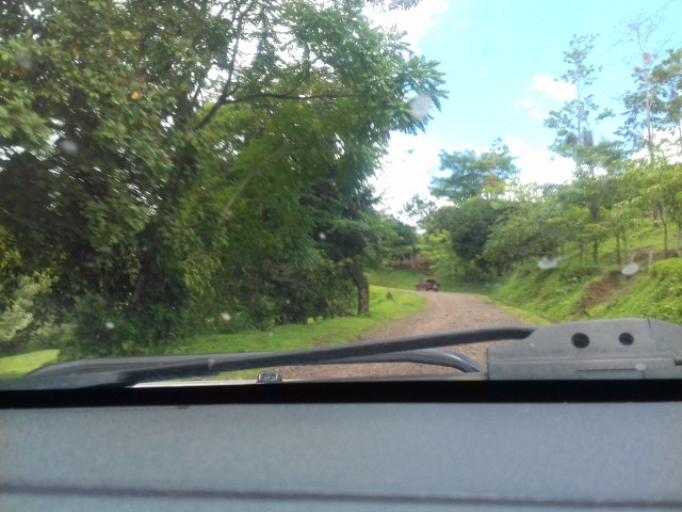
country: NI
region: Matagalpa
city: Rio Blanco
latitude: 12.9968
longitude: -85.1934
